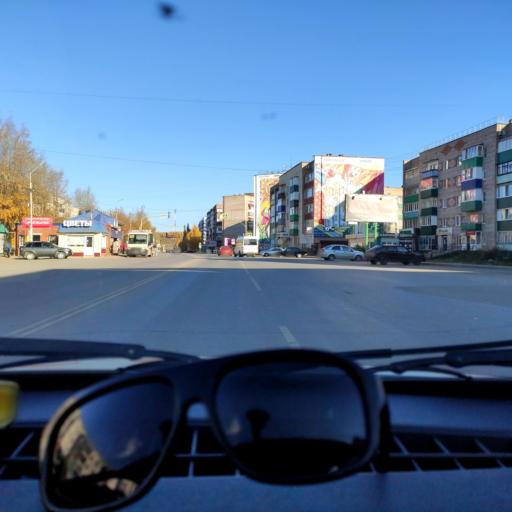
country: RU
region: Bashkortostan
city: Blagoveshchensk
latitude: 55.0484
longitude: 55.9562
